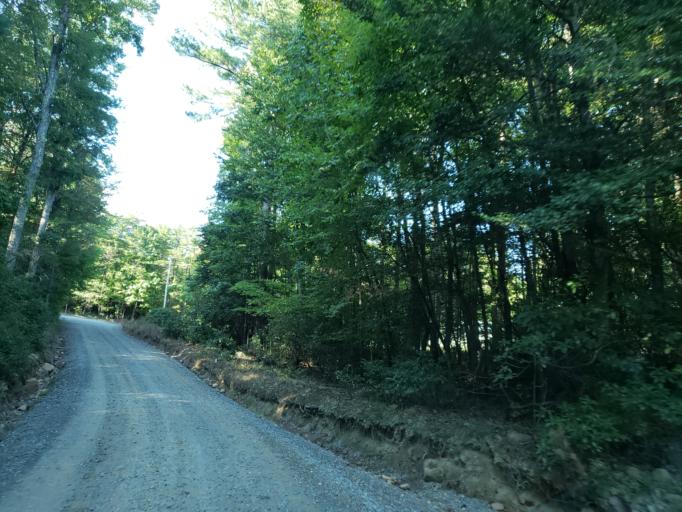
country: US
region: Georgia
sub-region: Fannin County
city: Blue Ridge
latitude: 34.6807
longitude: -84.2597
